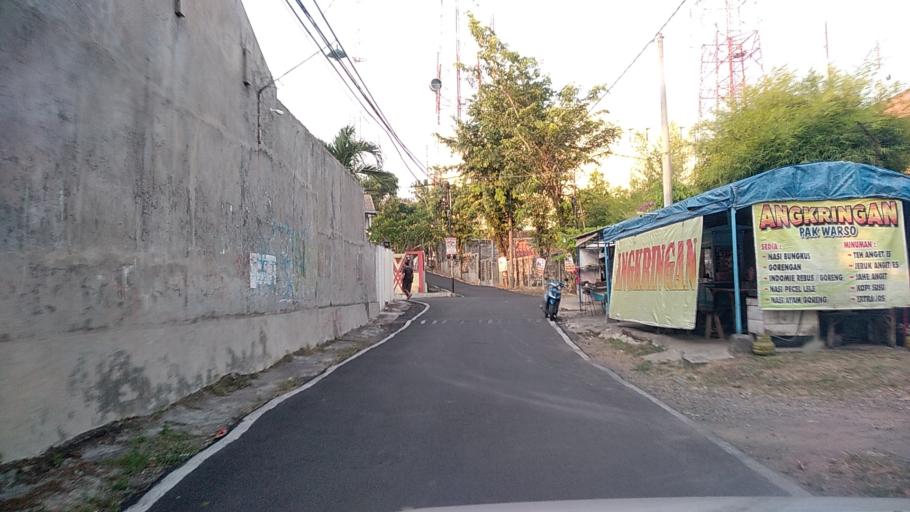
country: ID
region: Central Java
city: Semarang
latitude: -7.0464
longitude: 110.4232
